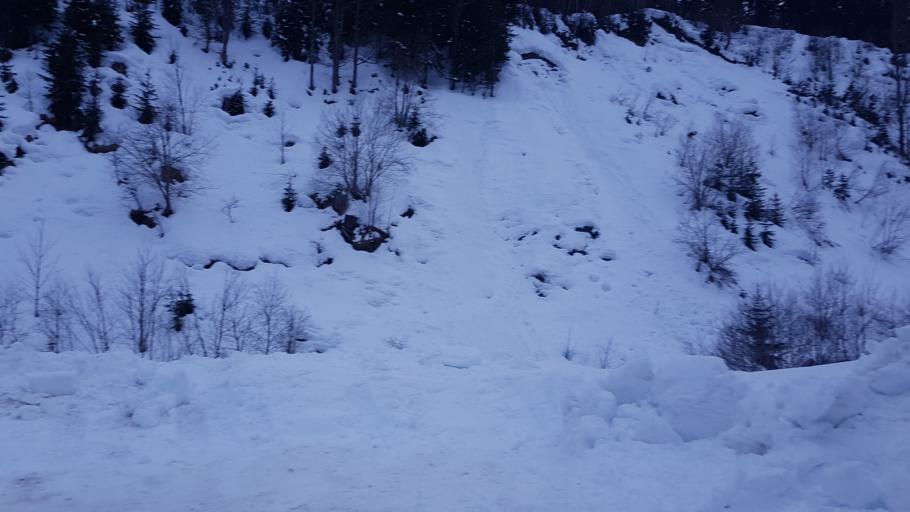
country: IT
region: Friuli Venezia Giulia
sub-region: Provincia di Udine
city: Malborghetto
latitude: 46.5471
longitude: 13.4695
